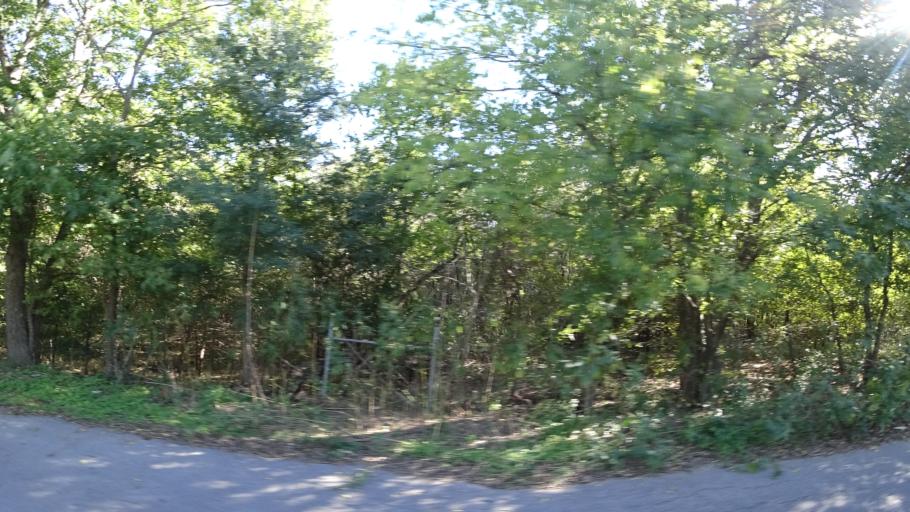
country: US
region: Texas
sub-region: Travis County
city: Austin
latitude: 30.2631
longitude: -97.6676
